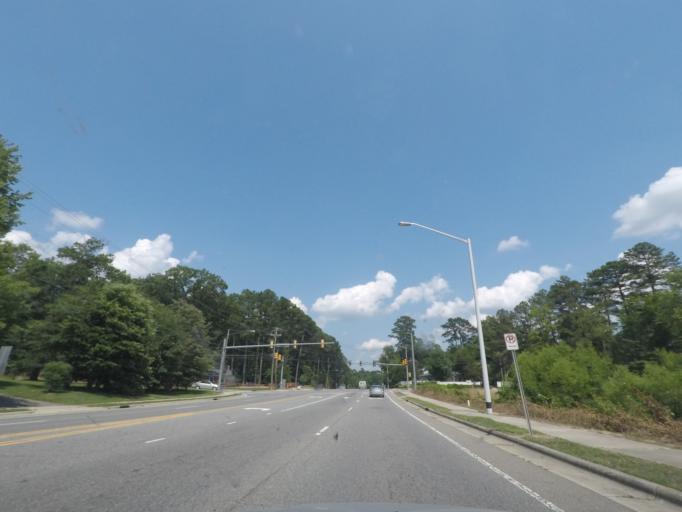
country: US
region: North Carolina
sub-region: Durham County
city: Durham
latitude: 35.9584
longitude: -78.9404
